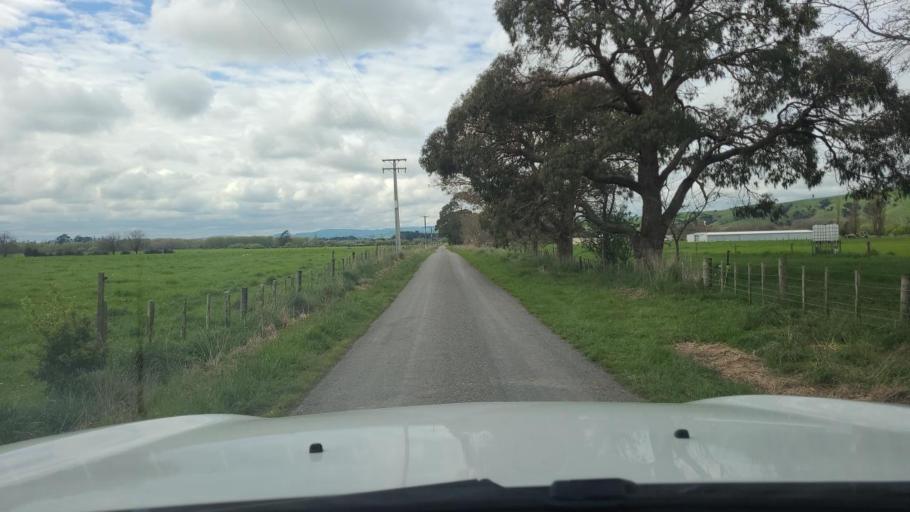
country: NZ
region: Wellington
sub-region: Masterton District
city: Masterton
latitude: -41.0957
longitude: 175.4894
